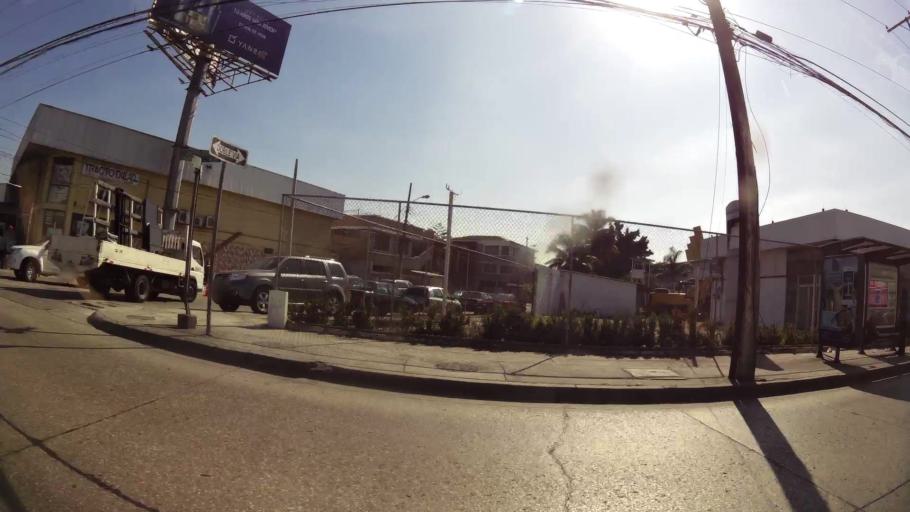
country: EC
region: Guayas
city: Eloy Alfaro
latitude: -2.1481
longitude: -79.9034
